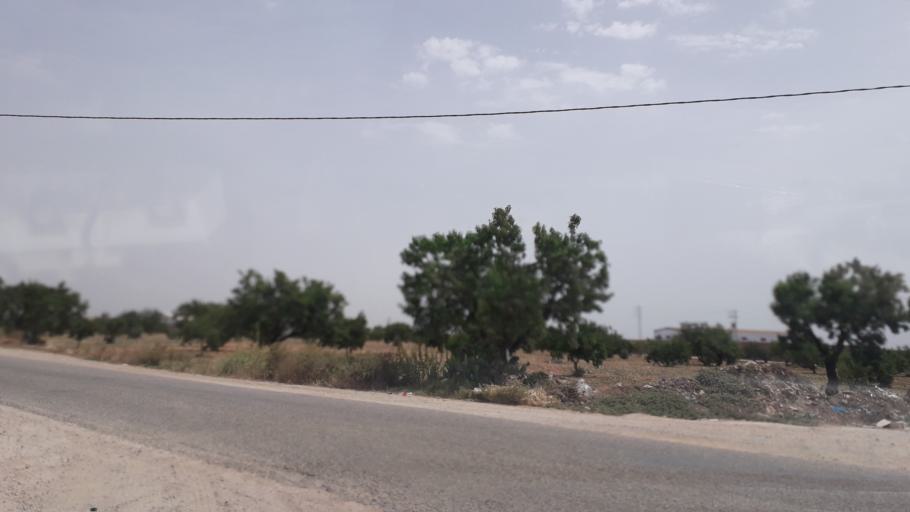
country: TN
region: Safaqis
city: Al Qarmadah
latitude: 34.8347
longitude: 10.7815
